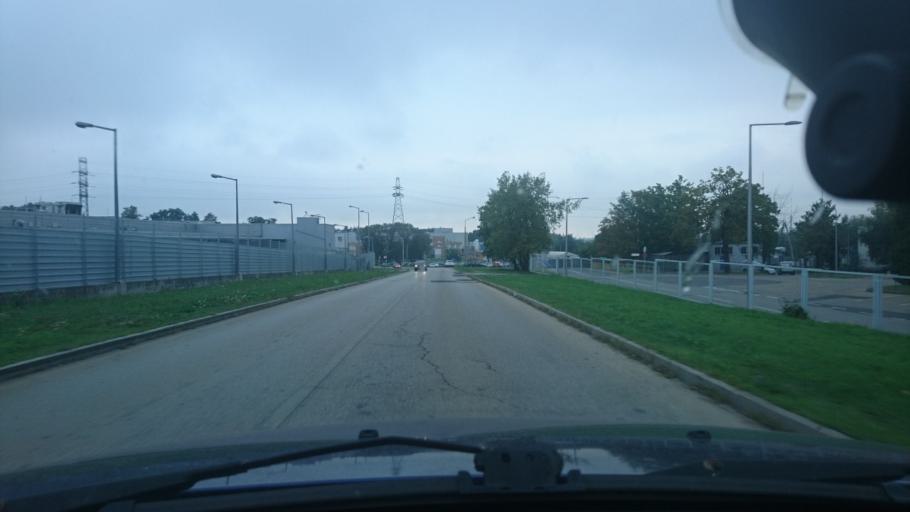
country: PL
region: Silesian Voivodeship
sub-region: Bielsko-Biala
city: Bielsko-Biala
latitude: 49.8449
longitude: 19.0380
